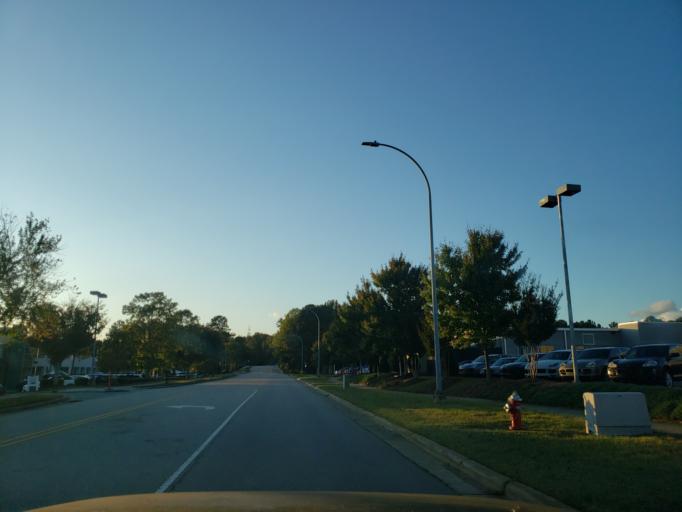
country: US
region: North Carolina
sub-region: Wake County
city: Apex
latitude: 35.7398
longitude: -78.8143
